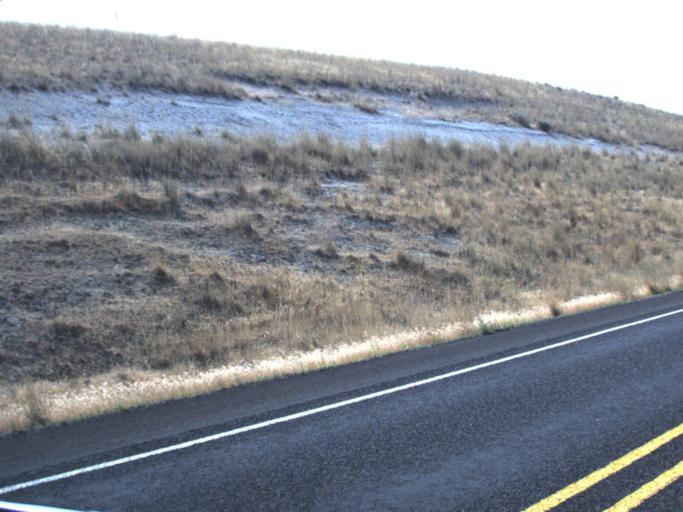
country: US
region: Washington
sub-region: Grant County
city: Desert Aire
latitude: 46.5477
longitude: -119.8325
